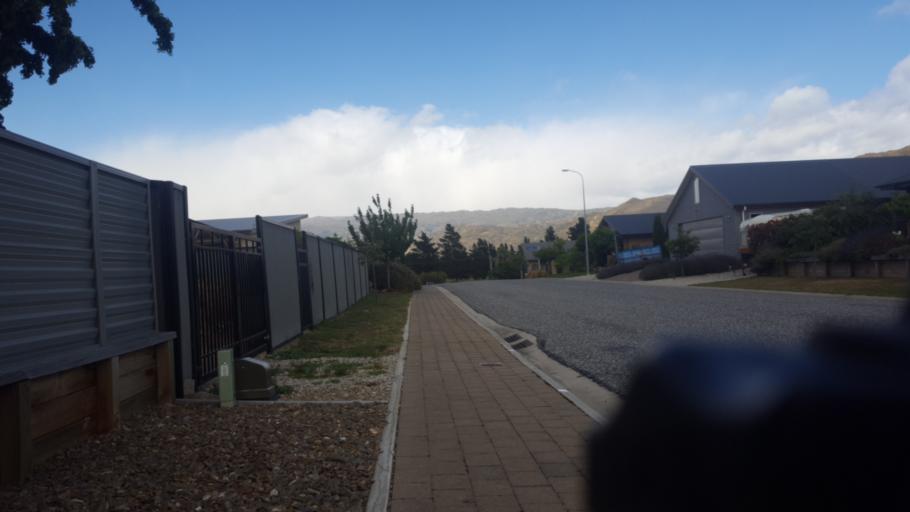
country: NZ
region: Otago
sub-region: Queenstown-Lakes District
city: Wanaka
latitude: -45.1954
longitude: 169.3309
